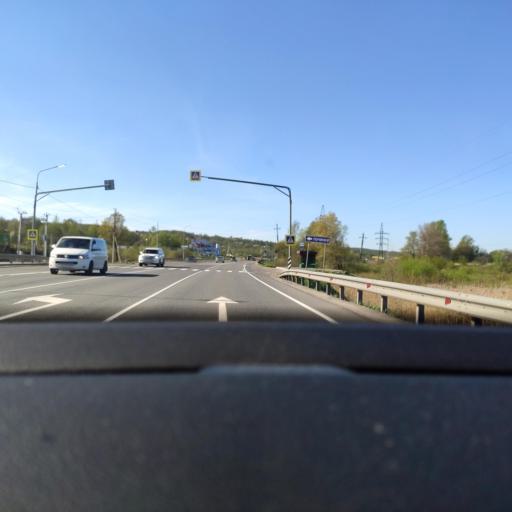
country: RU
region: Moskovskaya
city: Yakhroma
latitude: 56.3020
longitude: 37.4811
